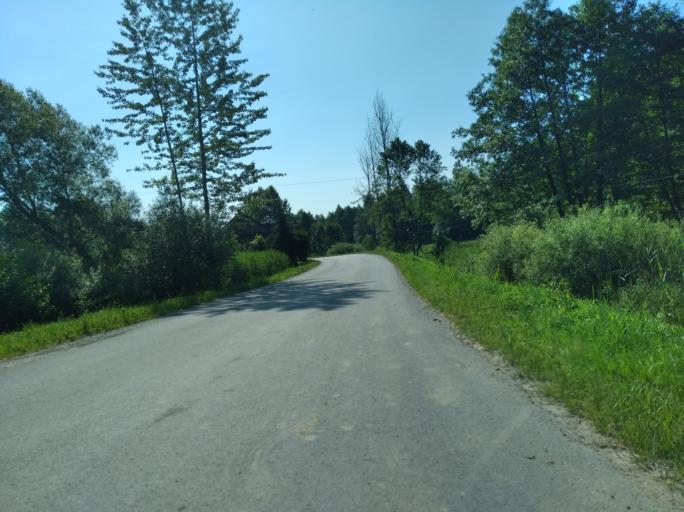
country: PL
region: Subcarpathian Voivodeship
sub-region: Powiat brzozowski
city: Wesola
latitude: 49.8276
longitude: 22.1537
